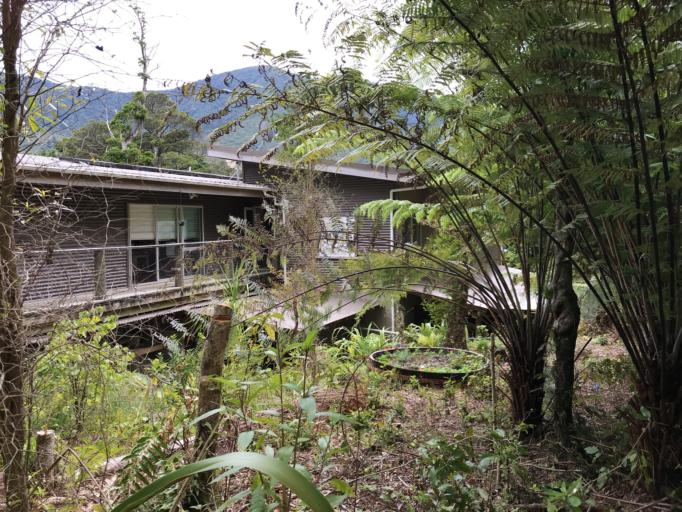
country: NZ
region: Marlborough
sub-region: Marlborough District
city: Picton
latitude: -41.0940
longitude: 174.1881
